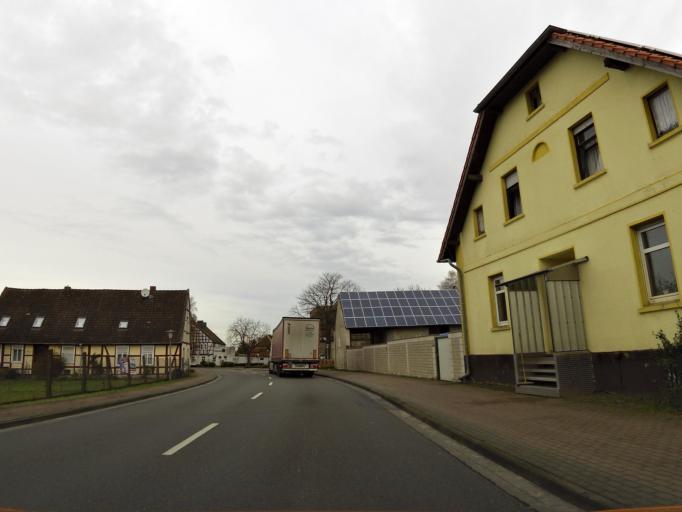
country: DE
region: Saxony-Anhalt
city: Pretzier
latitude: 52.7924
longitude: 11.2332
